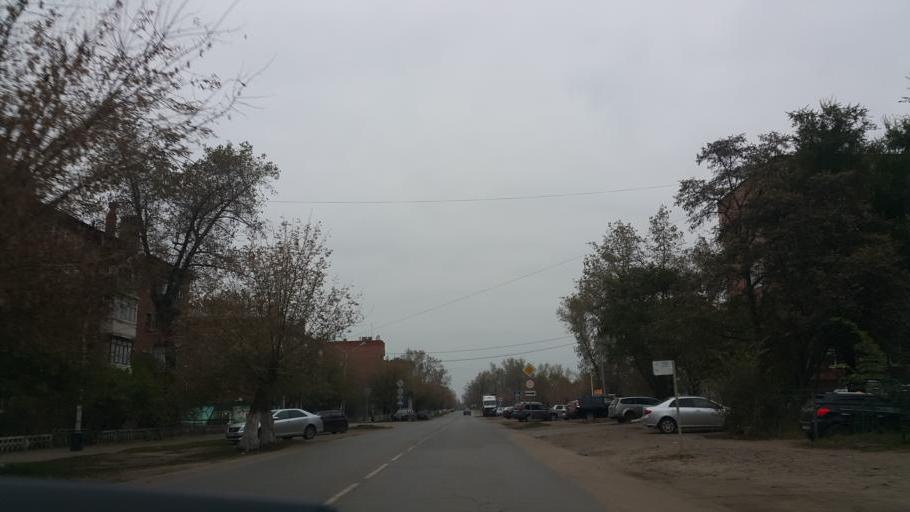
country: RU
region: Tambov
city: Kotovsk
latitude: 52.5894
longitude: 41.5025
